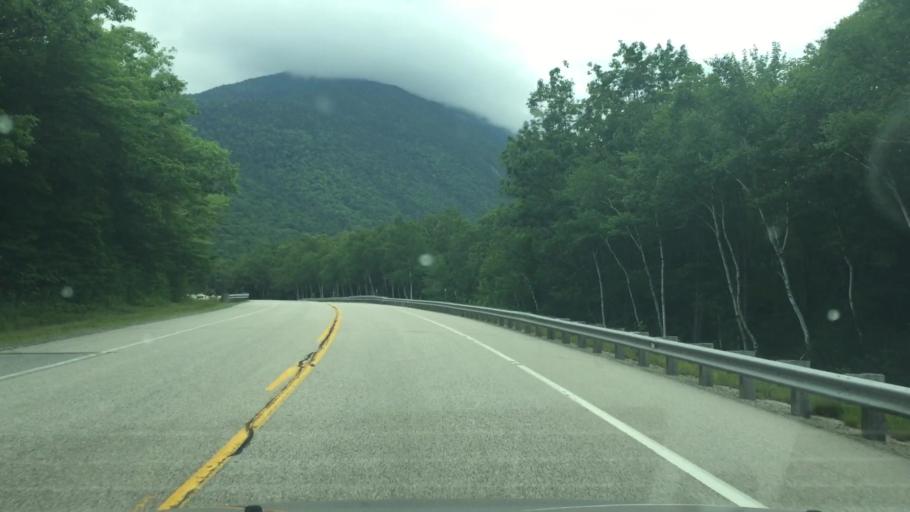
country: US
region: New Hampshire
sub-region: Grafton County
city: Deerfield
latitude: 44.1699
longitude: -71.3834
